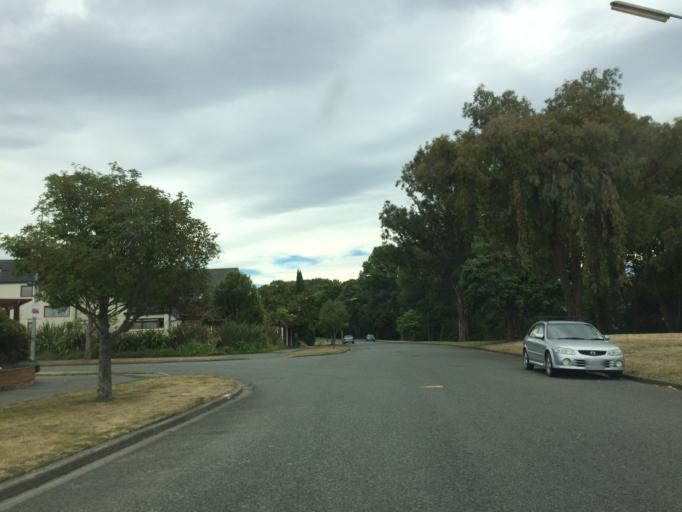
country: NZ
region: Canterbury
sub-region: Christchurch City
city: Christchurch
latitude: -43.5243
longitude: 172.5681
